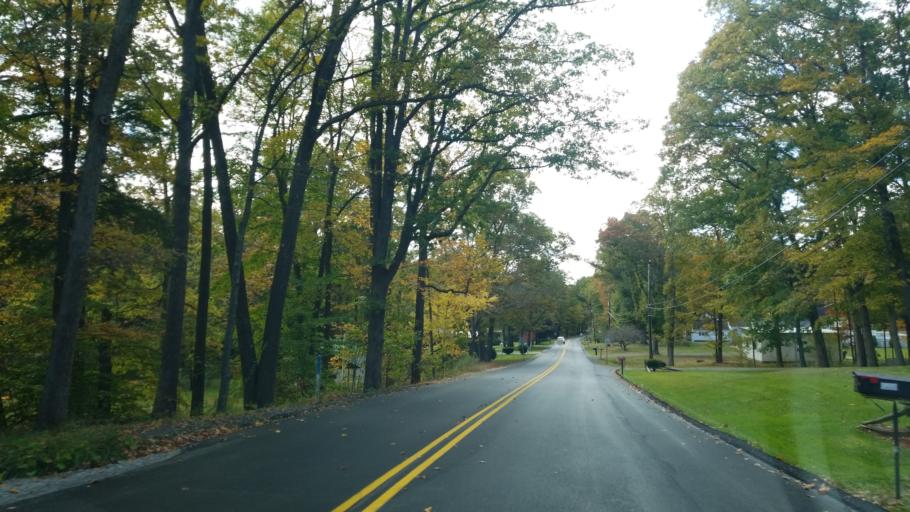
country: US
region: Pennsylvania
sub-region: Clearfield County
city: Sandy
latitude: 41.0914
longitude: -78.7872
